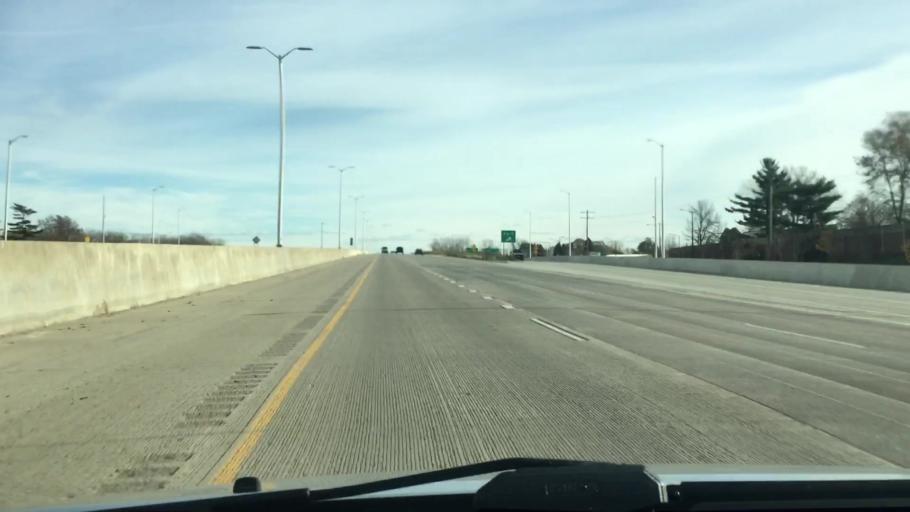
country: US
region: Wisconsin
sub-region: Brown County
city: Howard
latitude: 44.5455
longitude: -88.0943
